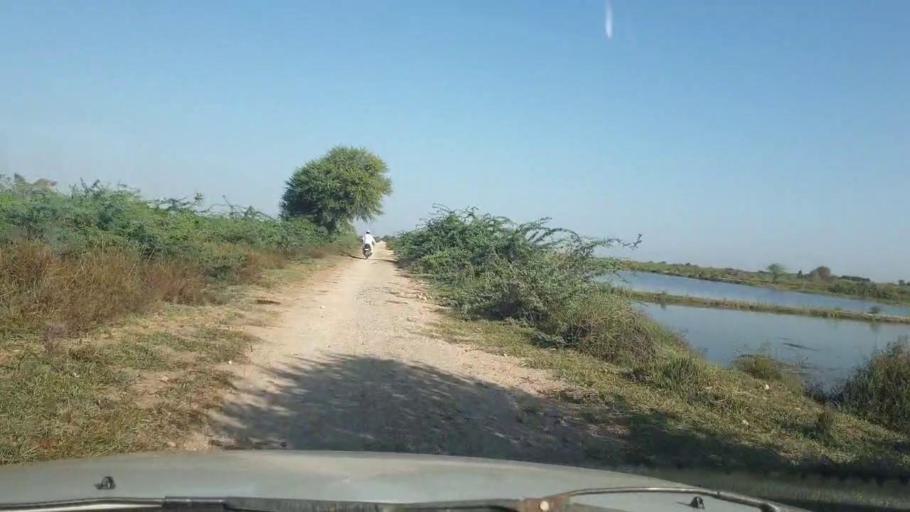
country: PK
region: Sindh
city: Chuhar Jamali
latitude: 24.5475
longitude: 67.9106
